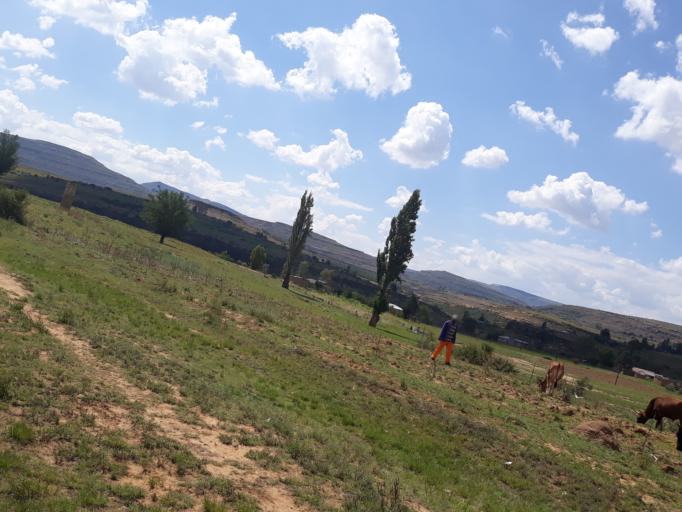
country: LS
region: Quthing
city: Quthing
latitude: -30.3398
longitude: 27.5297
